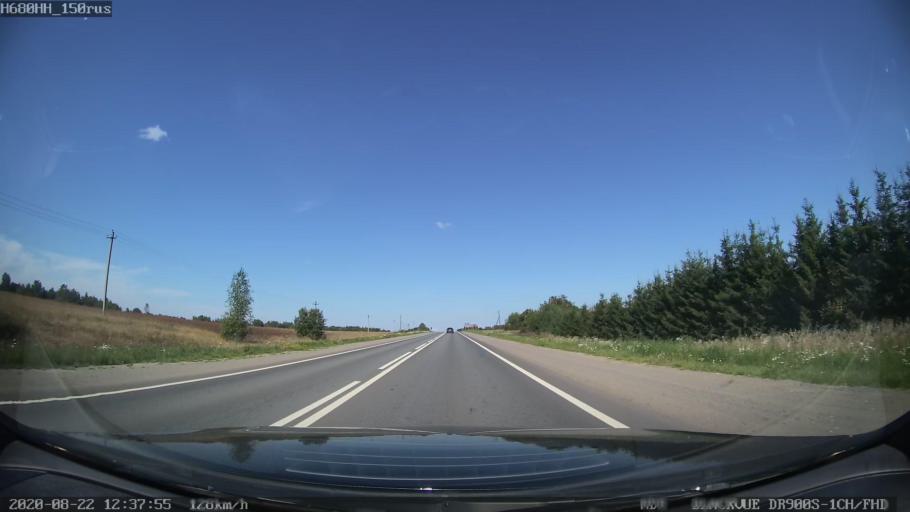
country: RU
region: Tverskaya
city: Rameshki
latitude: 57.3059
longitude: 36.0889
